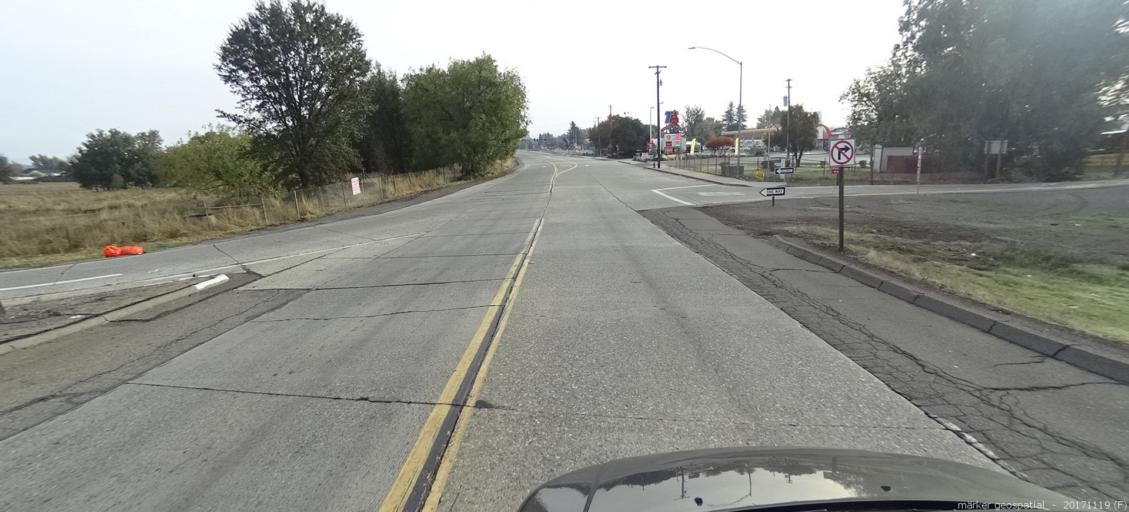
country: US
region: California
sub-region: Shasta County
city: Anderson
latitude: 40.5055
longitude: -122.3367
